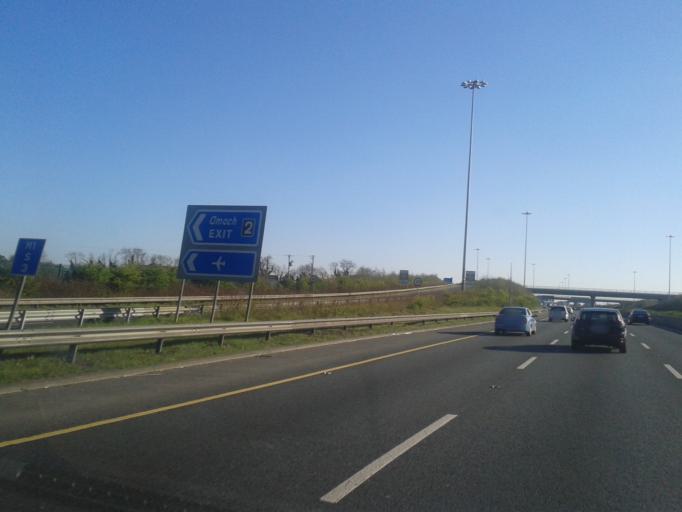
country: IE
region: Leinster
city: Kinsealy-Drinan
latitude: 53.4305
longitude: -6.2153
